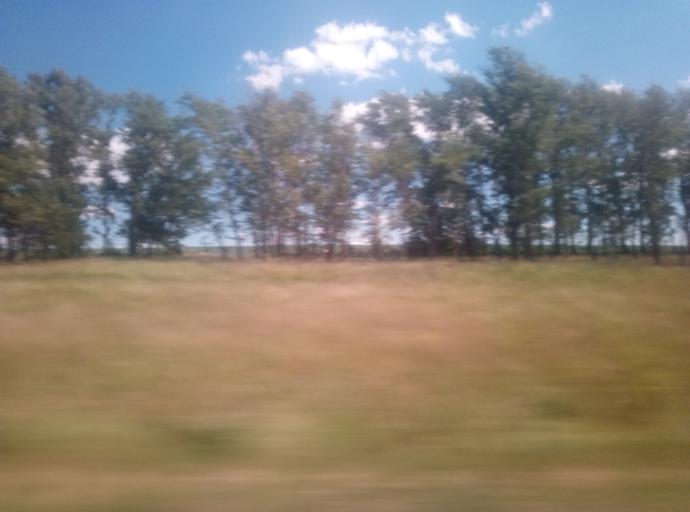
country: RU
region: Tula
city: Kireyevsk
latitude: 53.9411
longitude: 37.9488
